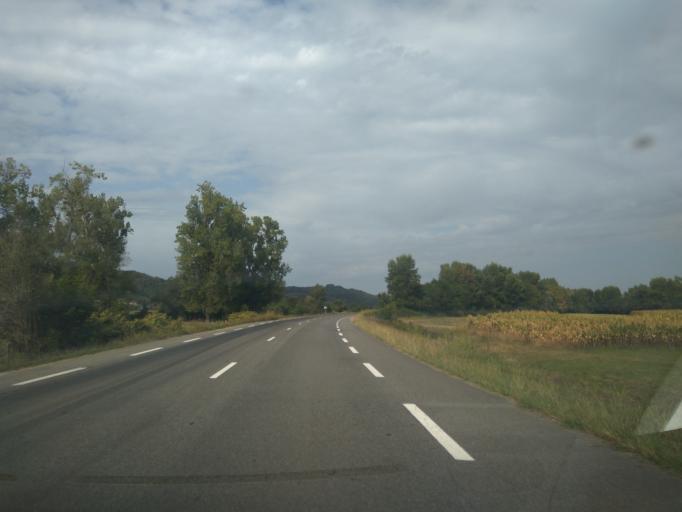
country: FR
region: Aquitaine
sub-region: Departement des Pyrenees-Atlantiques
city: Arbus
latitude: 43.3324
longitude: -0.4906
